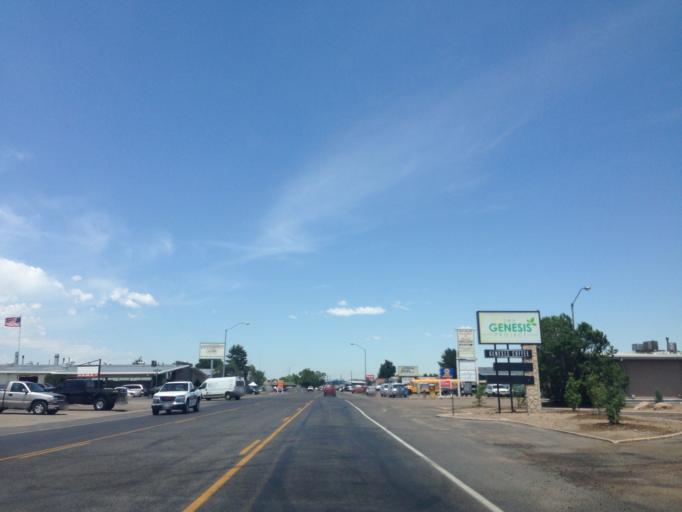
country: US
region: Colorado
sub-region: Larimer County
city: Fort Collins
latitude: 40.5827
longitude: -105.0502
